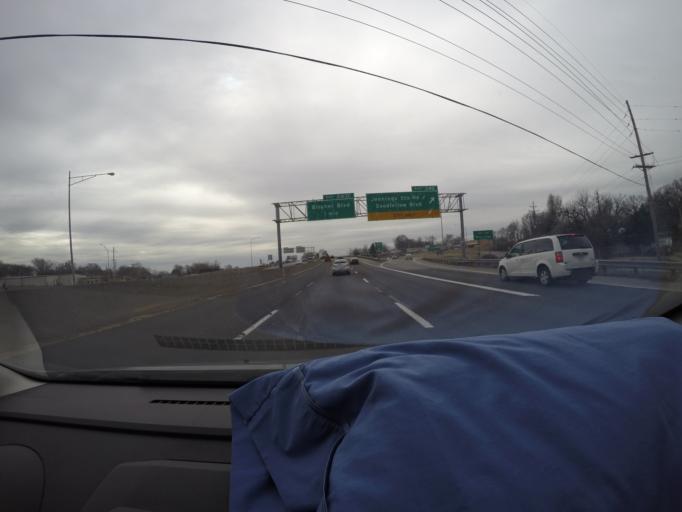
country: US
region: Missouri
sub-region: Saint Louis County
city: Pine Lawn
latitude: 38.7047
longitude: -90.2709
